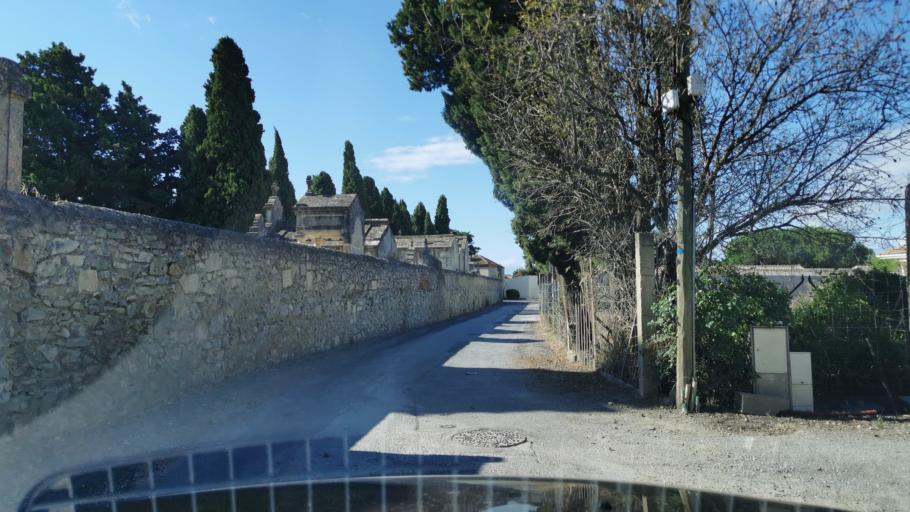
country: FR
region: Languedoc-Roussillon
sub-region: Departement de l'Aude
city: Marcorignan
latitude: 43.2482
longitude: 2.8988
